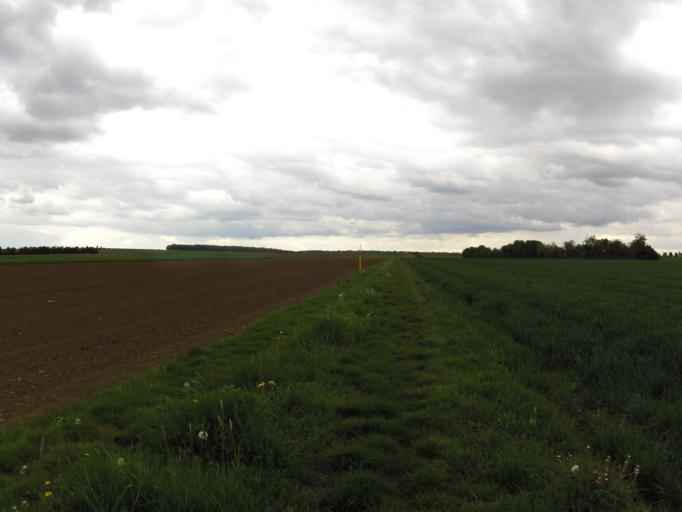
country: DE
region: Bavaria
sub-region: Regierungsbezirk Unterfranken
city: Unterpleichfeld
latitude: 49.8597
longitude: 10.0583
